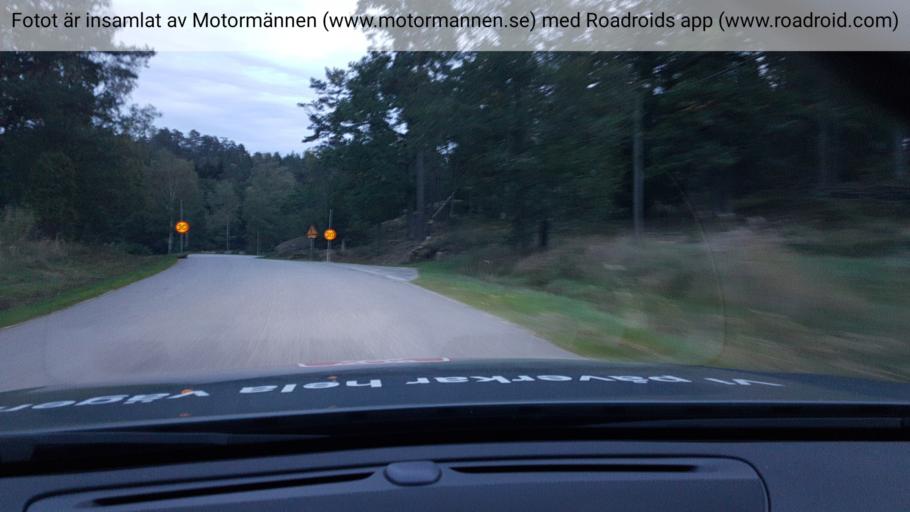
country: SE
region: Stockholm
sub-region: Haninge Kommun
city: Haninge
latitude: 59.0984
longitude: 18.2676
